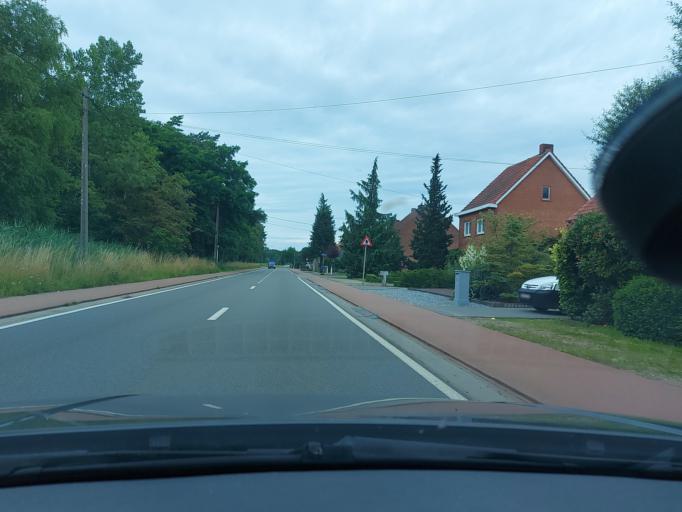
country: BE
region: Flanders
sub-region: Provincie Antwerpen
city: Balen
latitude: 51.2059
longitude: 5.2227
